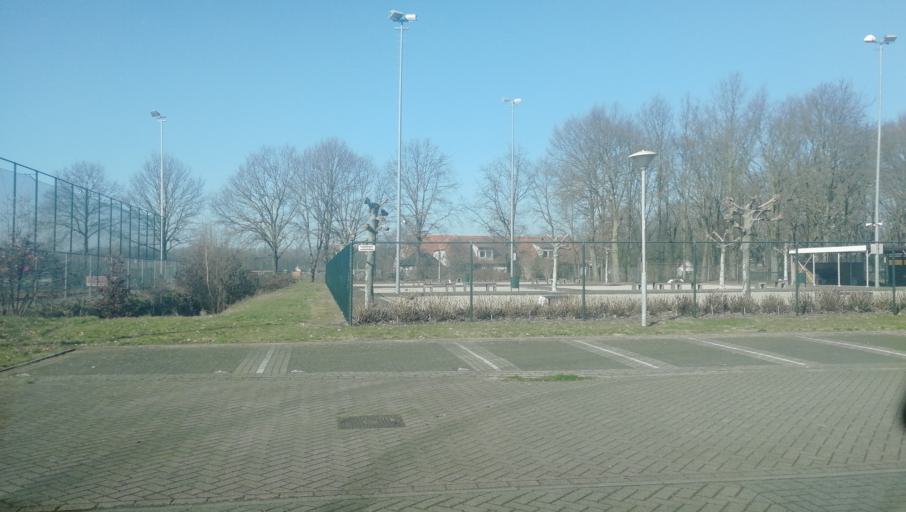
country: NL
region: Limburg
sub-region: Gemeente Venlo
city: Tegelen
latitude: 51.3728
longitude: 6.1172
